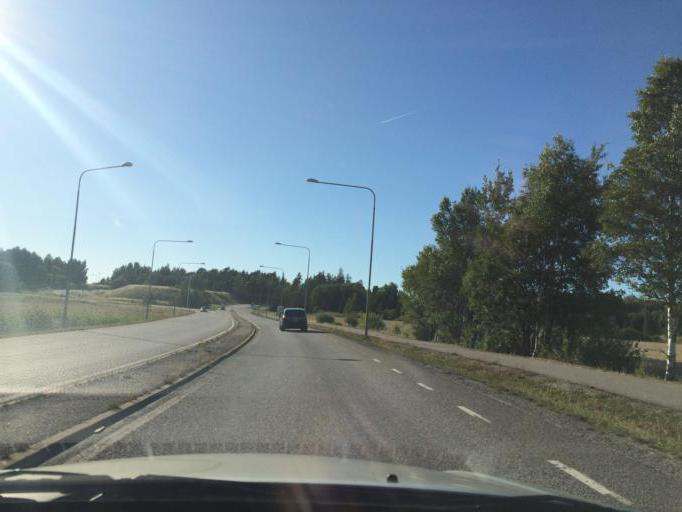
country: SE
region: Soedermanland
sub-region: Eskilstuna Kommun
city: Hallbybrunn
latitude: 59.3949
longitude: 16.4476
